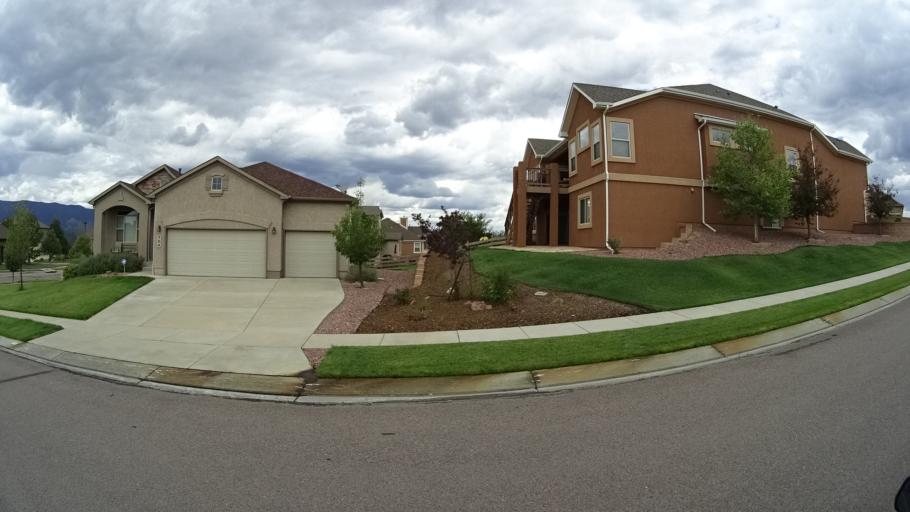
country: US
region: Colorado
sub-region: El Paso County
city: Gleneagle
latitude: 39.0301
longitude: -104.8134
